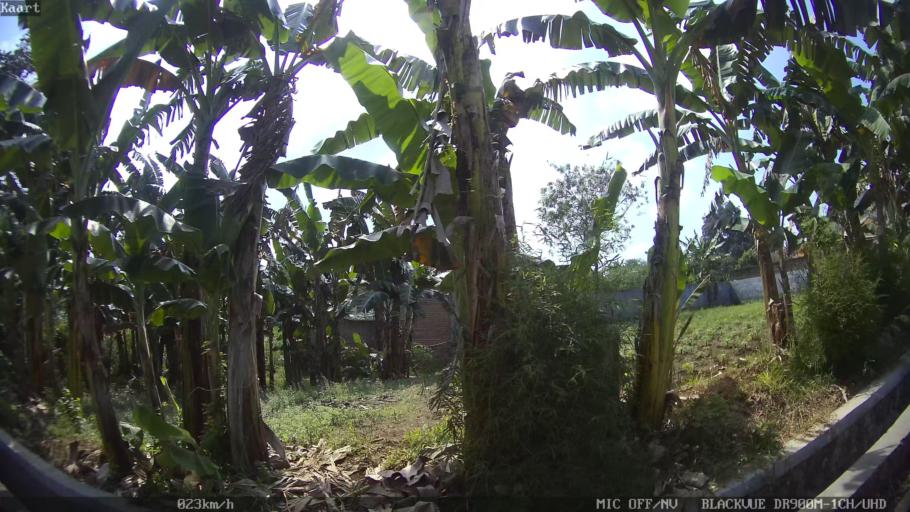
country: ID
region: Lampung
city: Kedaton
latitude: -5.3380
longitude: 105.2727
